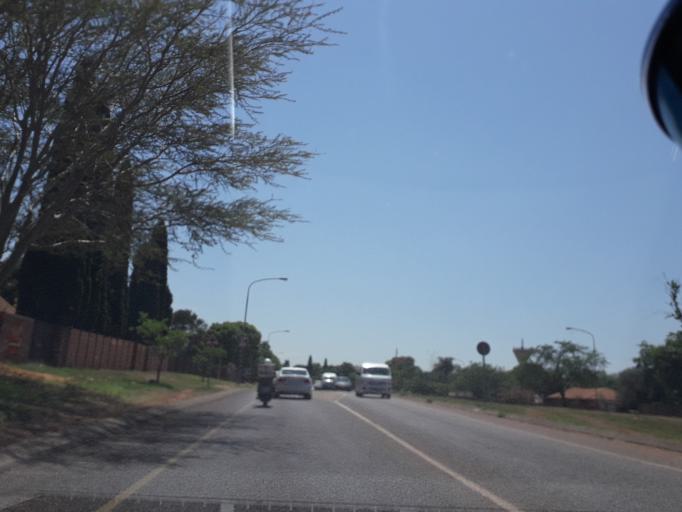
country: ZA
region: Gauteng
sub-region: City of Tshwane Metropolitan Municipality
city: Centurion
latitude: -25.8696
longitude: 28.1785
